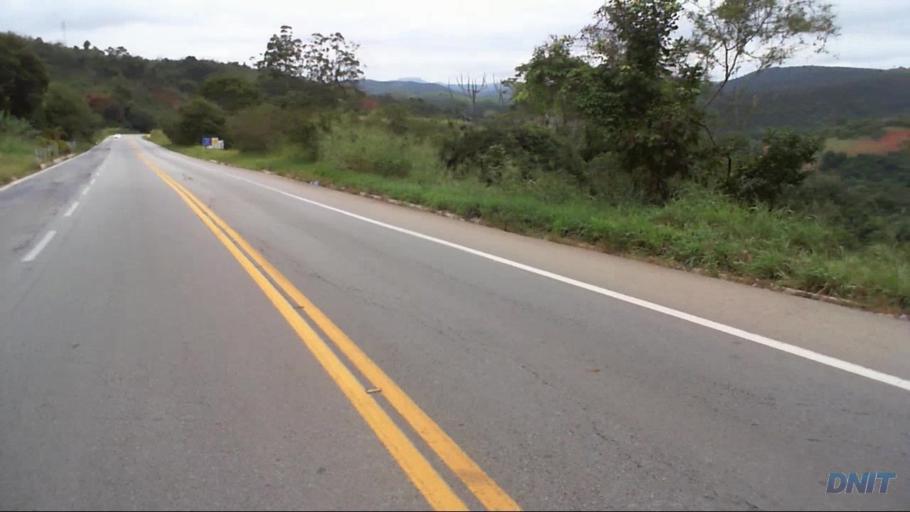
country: BR
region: Minas Gerais
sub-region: Nova Era
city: Nova Era
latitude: -19.7905
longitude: -43.0538
